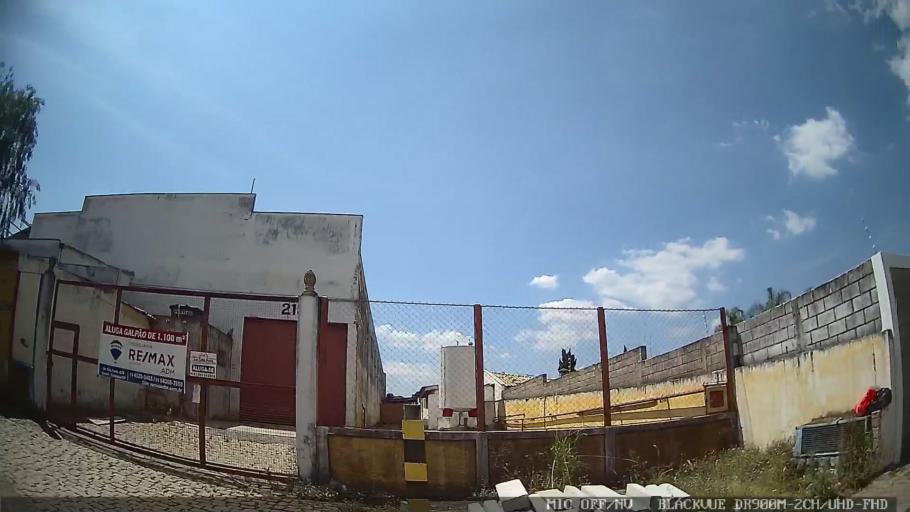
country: BR
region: Sao Paulo
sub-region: Itupeva
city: Itupeva
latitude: -23.2467
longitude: -47.0602
